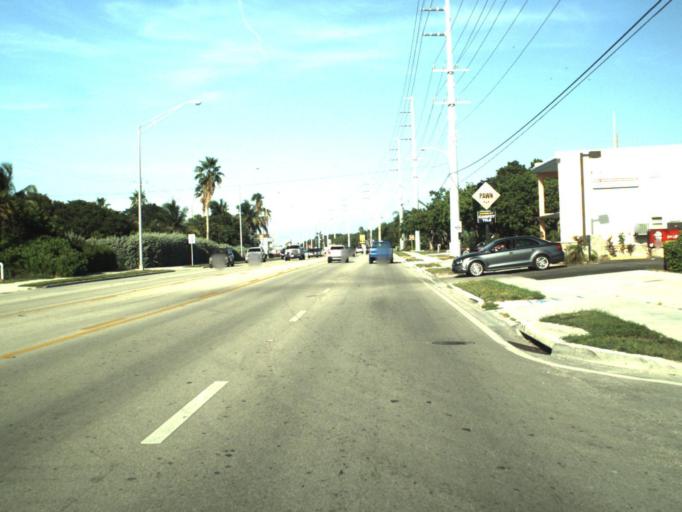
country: US
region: Florida
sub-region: Monroe County
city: Marathon
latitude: 24.7184
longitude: -81.0674
